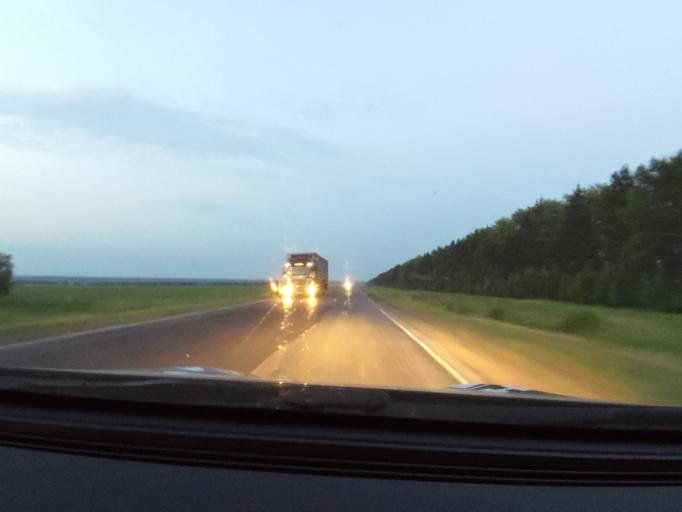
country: RU
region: Bashkortostan
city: Duvan
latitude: 56.0765
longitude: 58.1237
